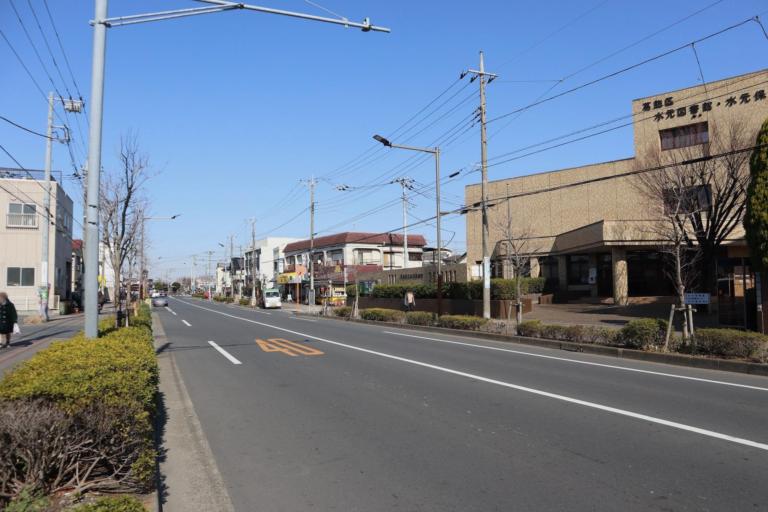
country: JP
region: Chiba
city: Matsudo
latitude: 35.7787
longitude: 139.8670
